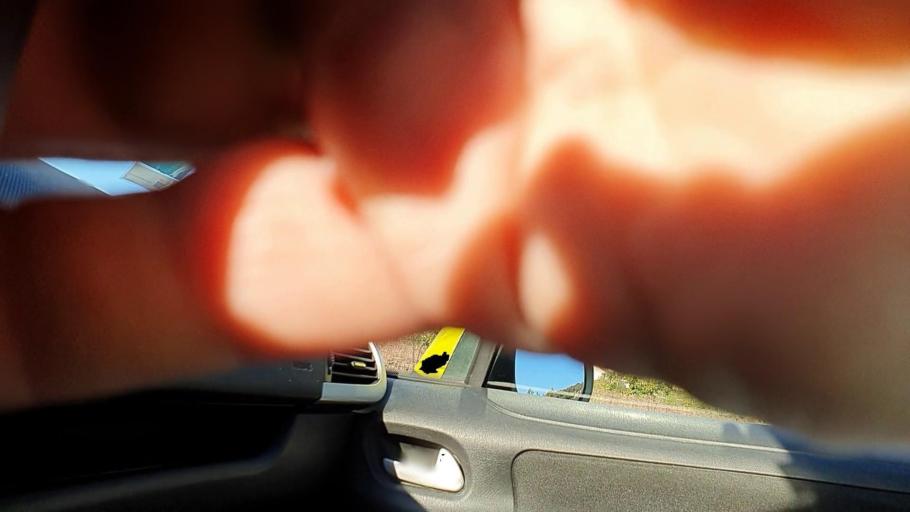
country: FR
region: Languedoc-Roussillon
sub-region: Departement du Gard
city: Saint-Julien-les-Rosiers
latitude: 44.1568
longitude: 4.1121
